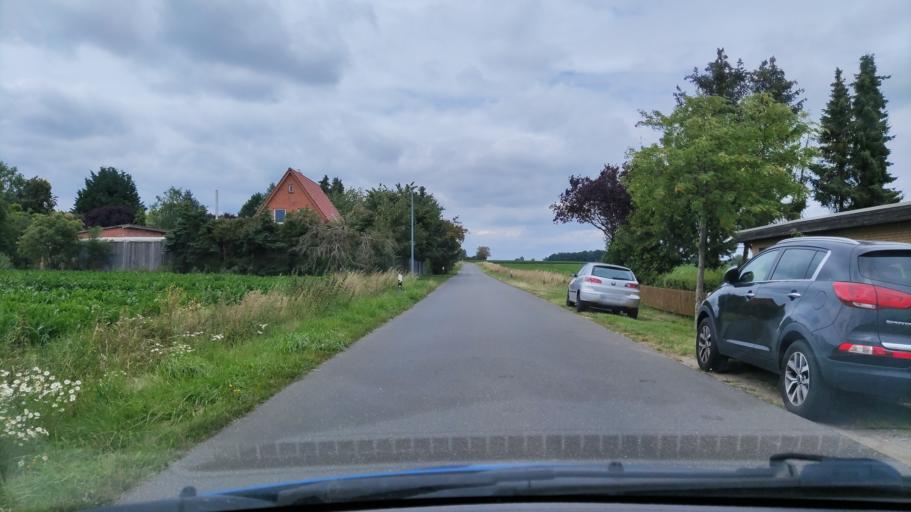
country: DE
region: Lower Saxony
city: Weste
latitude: 53.0638
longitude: 10.6992
